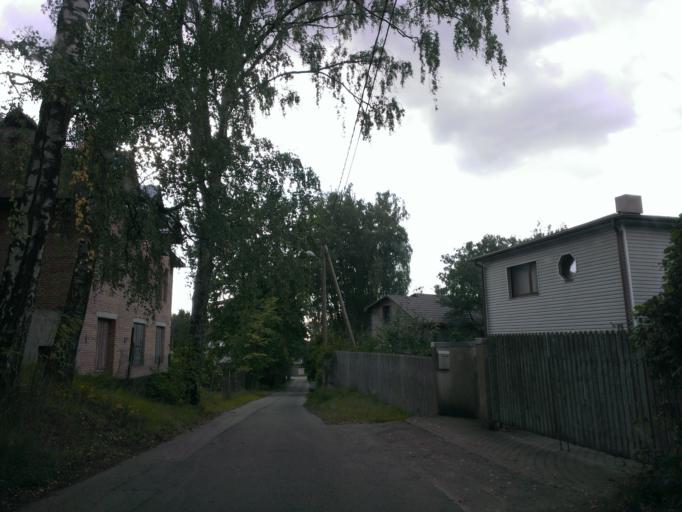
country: LV
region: Ikskile
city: Ikskile
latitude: 56.8368
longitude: 24.4898
